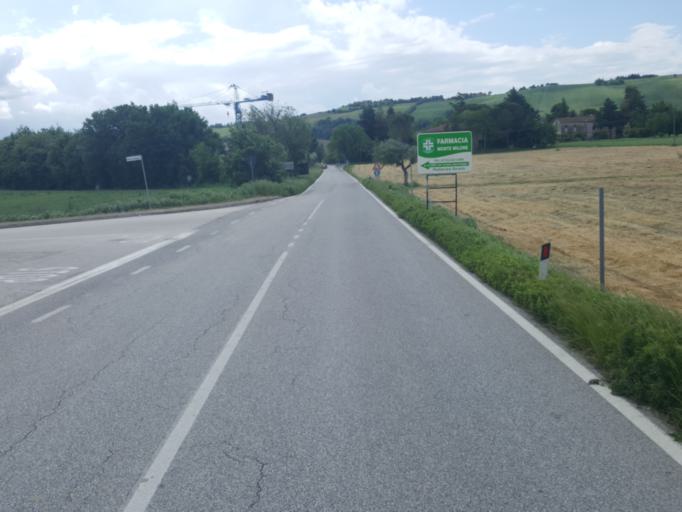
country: IT
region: The Marches
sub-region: Provincia di Macerata
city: Pollenza
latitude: 43.2379
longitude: 13.3662
